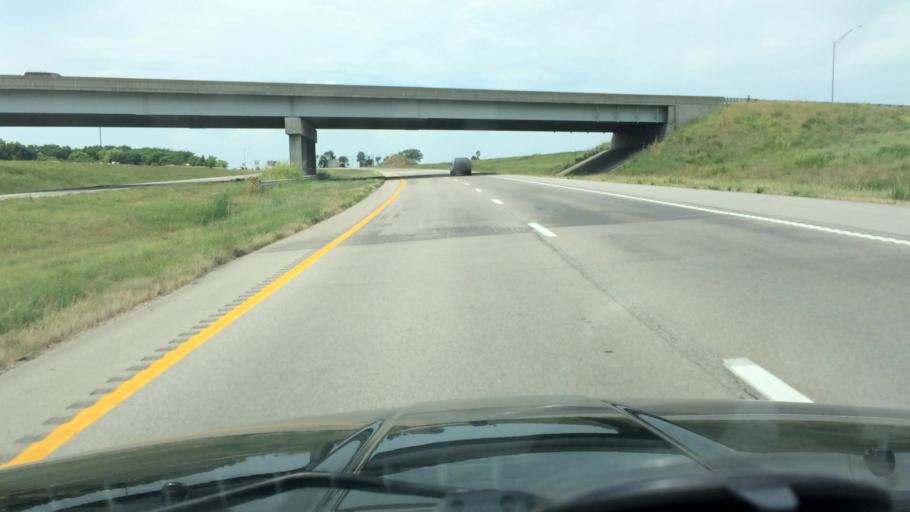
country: US
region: Missouri
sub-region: Polk County
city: Bolivar
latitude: 37.5745
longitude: -93.3979
